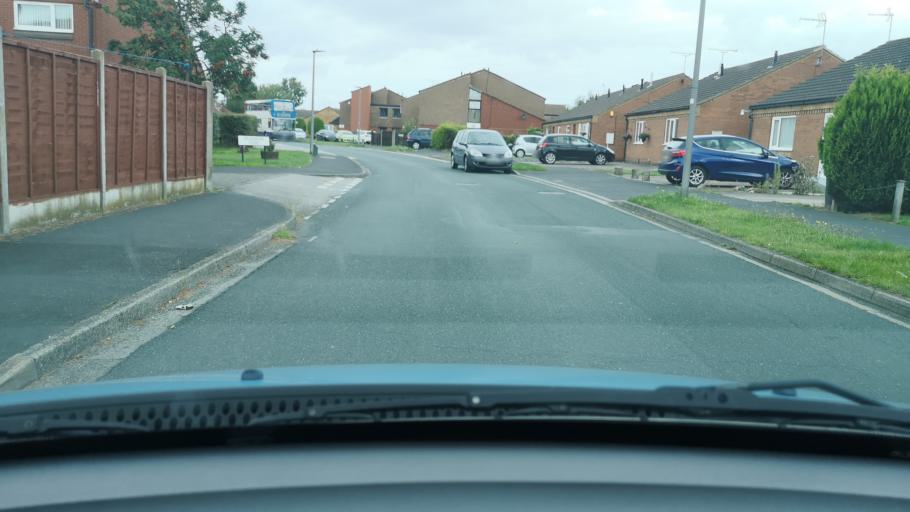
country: GB
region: England
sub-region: North Lincolnshire
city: Scunthorpe
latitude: 53.5869
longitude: -0.6885
